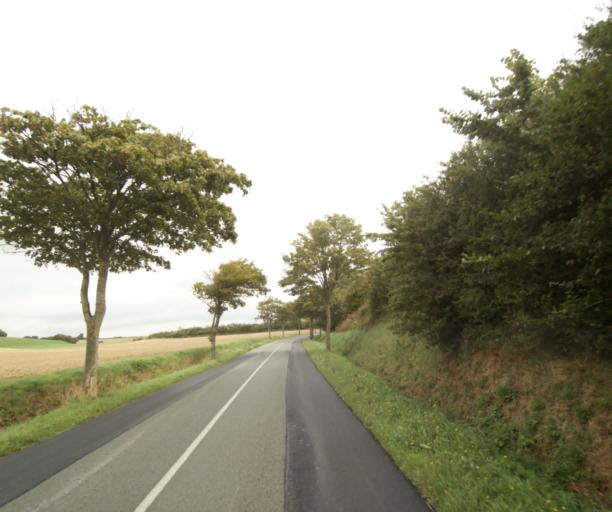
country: FR
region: Nord-Pas-de-Calais
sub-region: Departement du Pas-de-Calais
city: Etaples
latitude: 50.5209
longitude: 1.6728
